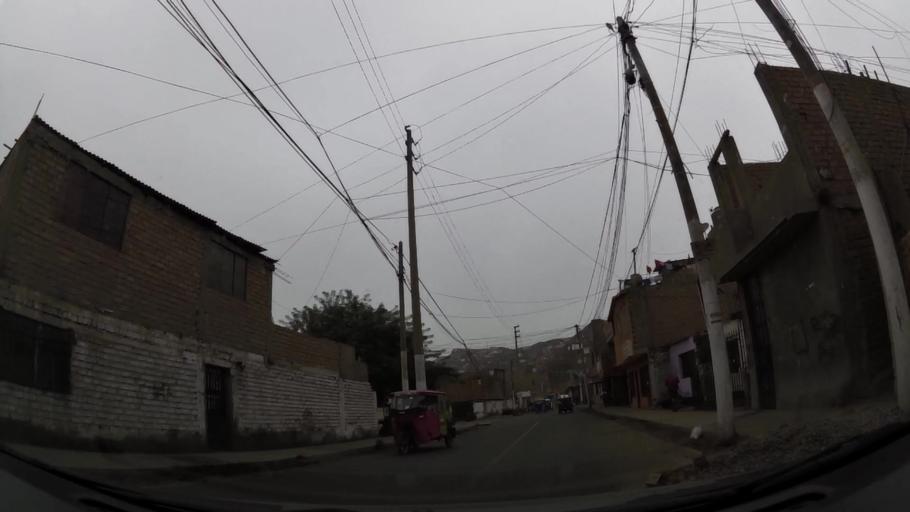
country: PE
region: Lima
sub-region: Lima
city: Carabayllo
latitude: -11.8698
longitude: -77.0757
